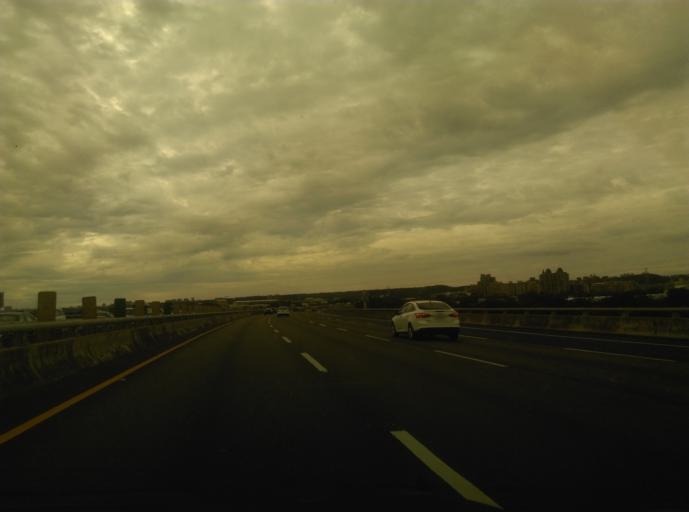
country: TW
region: Taiwan
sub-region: Taoyuan
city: Taoyuan
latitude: 24.9348
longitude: 121.3499
